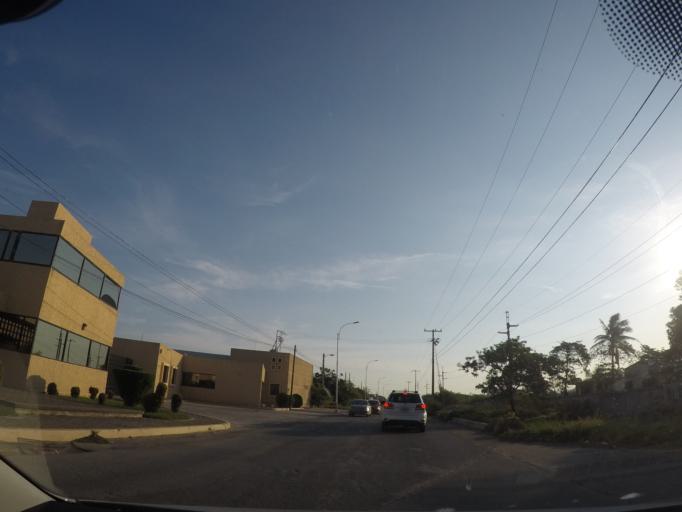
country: MX
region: Oaxaca
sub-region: Salina Cruz
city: Salina Cruz
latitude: 16.2146
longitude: -95.1927
